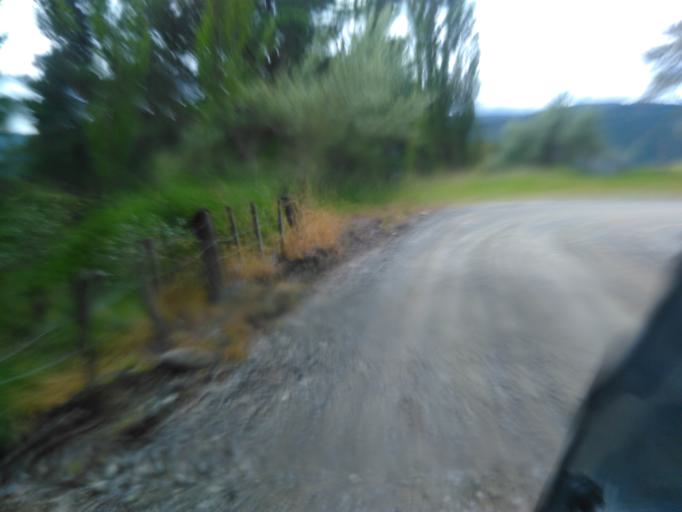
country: NZ
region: Gisborne
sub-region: Gisborne District
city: Gisborne
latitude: -38.0525
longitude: 178.1091
